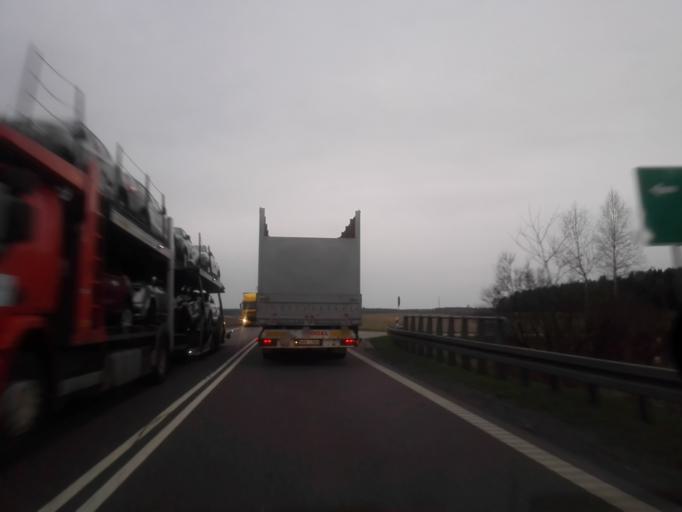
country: PL
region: Podlasie
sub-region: Powiat grajewski
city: Szczuczyn
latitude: 53.6029
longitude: 22.3633
